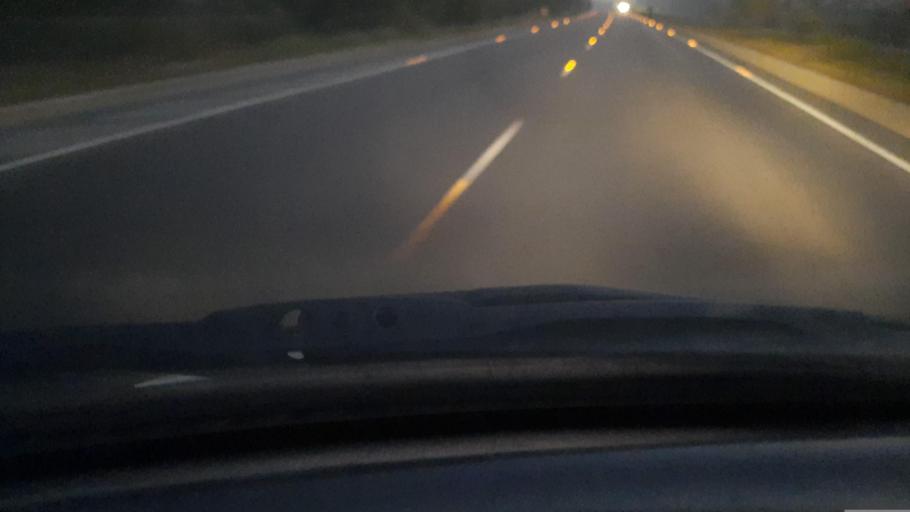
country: BD
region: Dhaka
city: Char Bhadrasan
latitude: 23.3997
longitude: 90.1808
